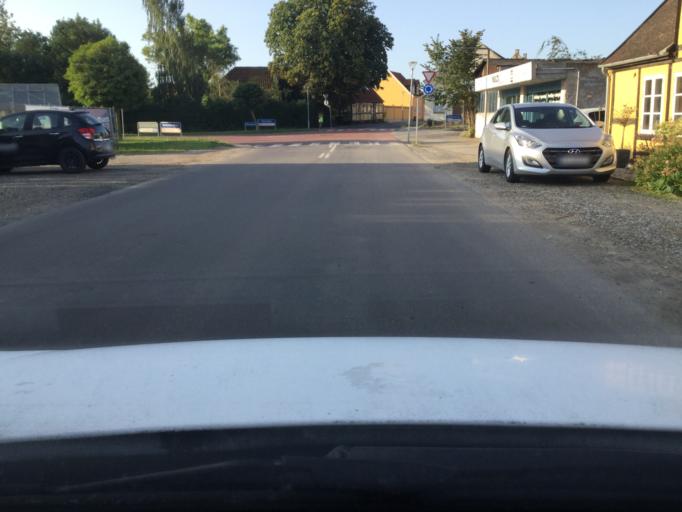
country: DK
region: Zealand
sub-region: Lolland Kommune
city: Rodby
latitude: 54.6976
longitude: 11.3880
